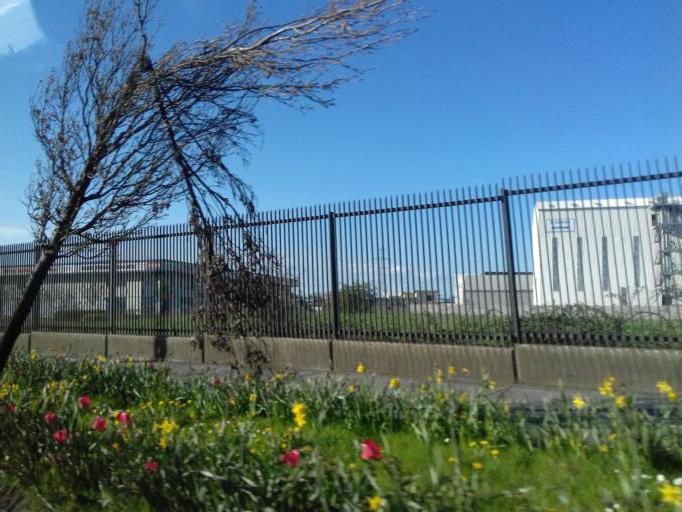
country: IE
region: Leinster
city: Castleknock
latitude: 53.4051
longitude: -6.3418
